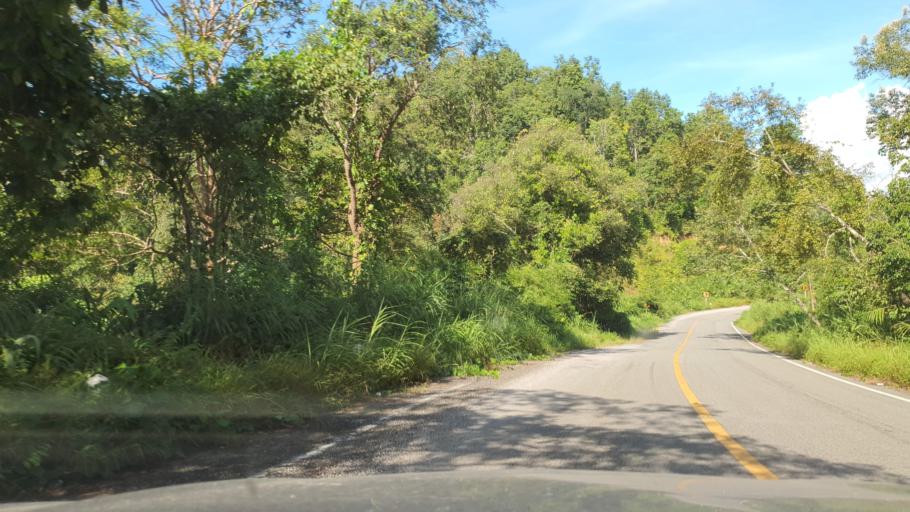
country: TH
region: Chiang Rai
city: Wiang Pa Pao
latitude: 19.3312
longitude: 99.4519
